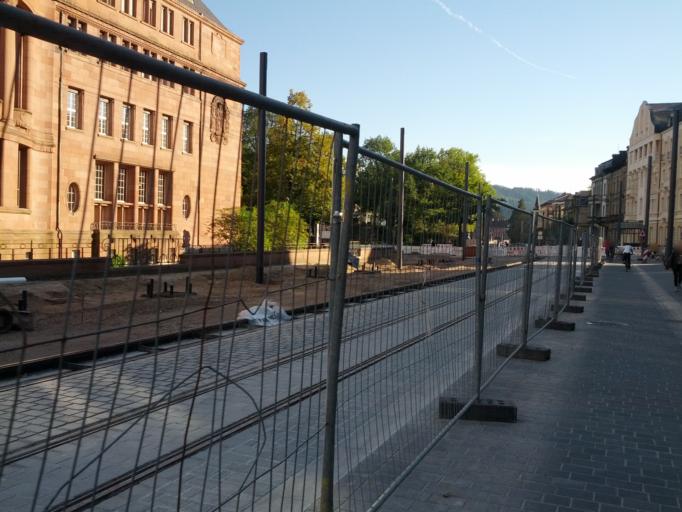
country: DE
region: Baden-Wuerttemberg
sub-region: Freiburg Region
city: Freiburg
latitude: 47.9944
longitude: 7.8455
